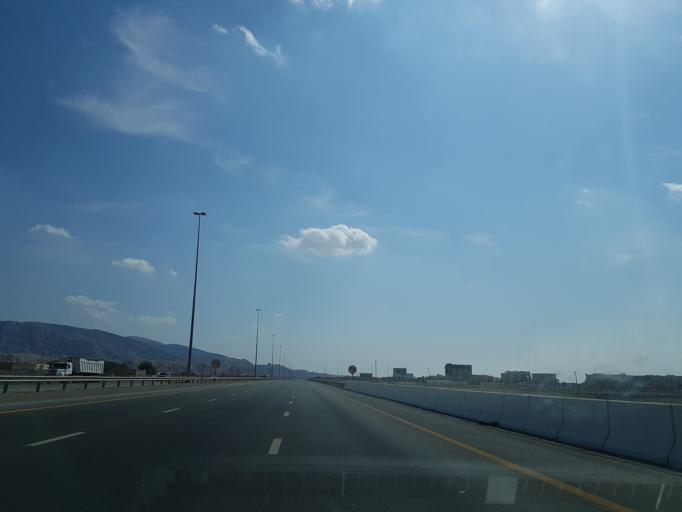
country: AE
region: Ra's al Khaymah
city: Ras al-Khaimah
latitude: 25.7994
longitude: 56.0305
